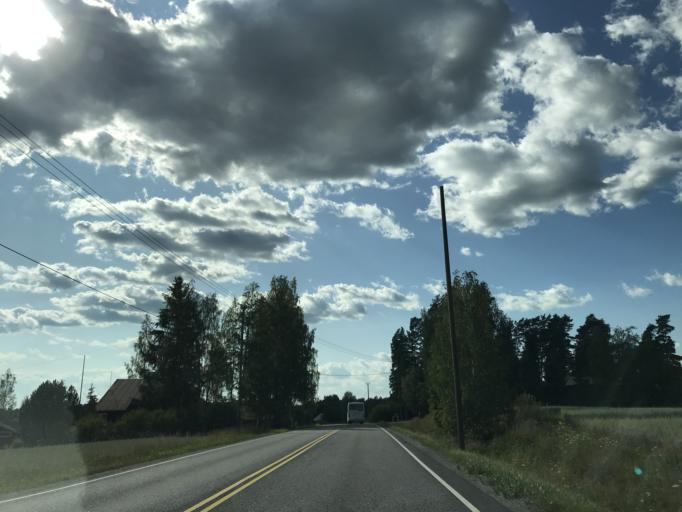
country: FI
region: Uusimaa
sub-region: Helsinki
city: Nurmijaervi
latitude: 60.4588
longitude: 24.7318
